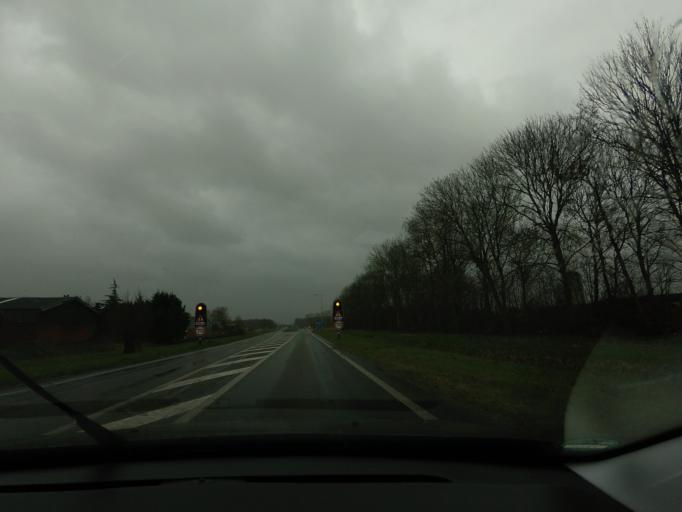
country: NL
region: Friesland
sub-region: Sudwest Fryslan
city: Bolsward
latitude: 53.0651
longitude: 5.5092
